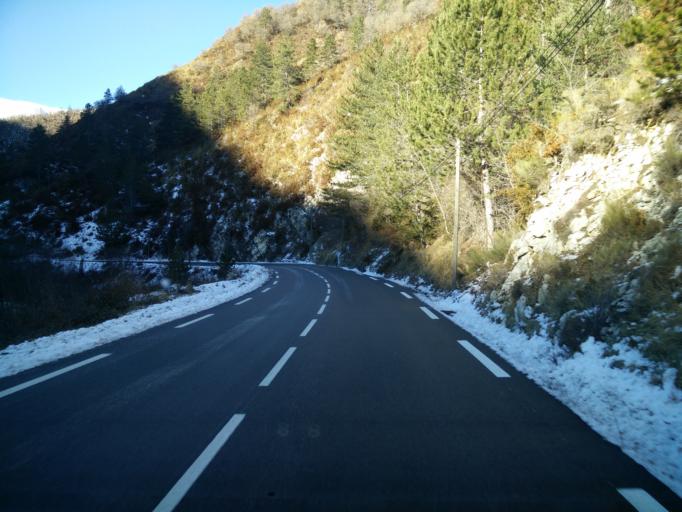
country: FR
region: Provence-Alpes-Cote d'Azur
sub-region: Departement des Alpes-de-Haute-Provence
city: Annot
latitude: 43.9328
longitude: 6.6514
